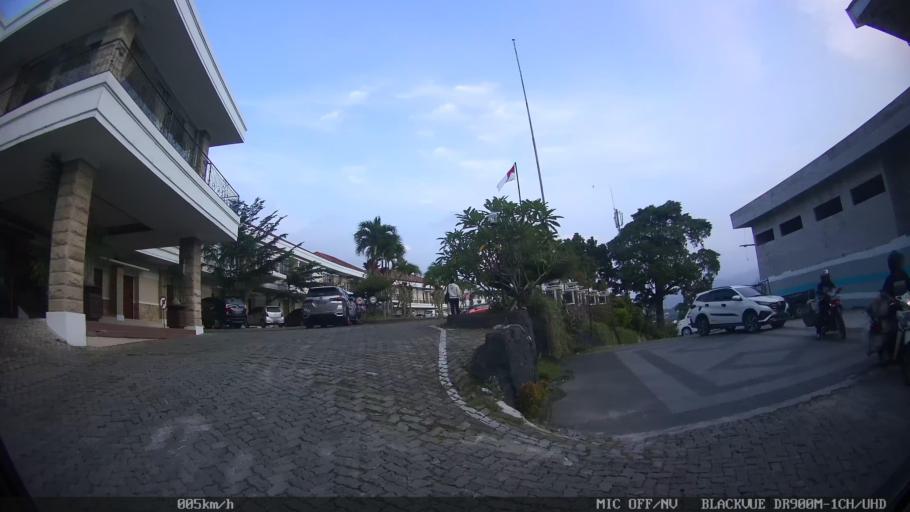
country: ID
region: Lampung
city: Bandarlampung
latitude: -5.4112
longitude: 105.2637
